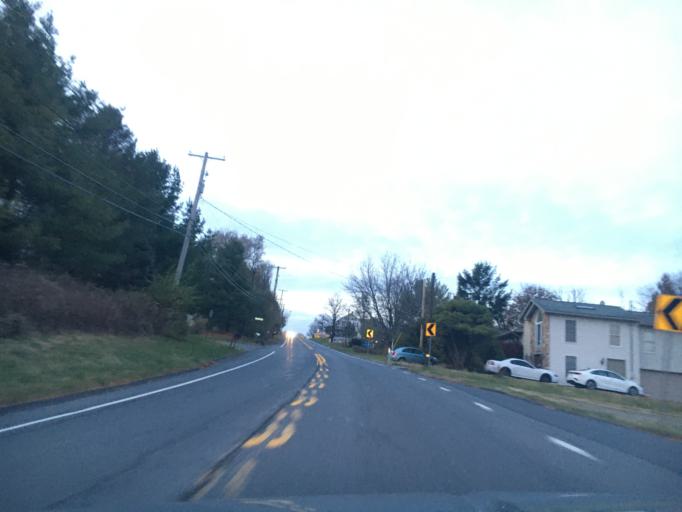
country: US
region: Pennsylvania
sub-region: Lehigh County
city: Egypt
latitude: 40.6749
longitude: -75.5685
